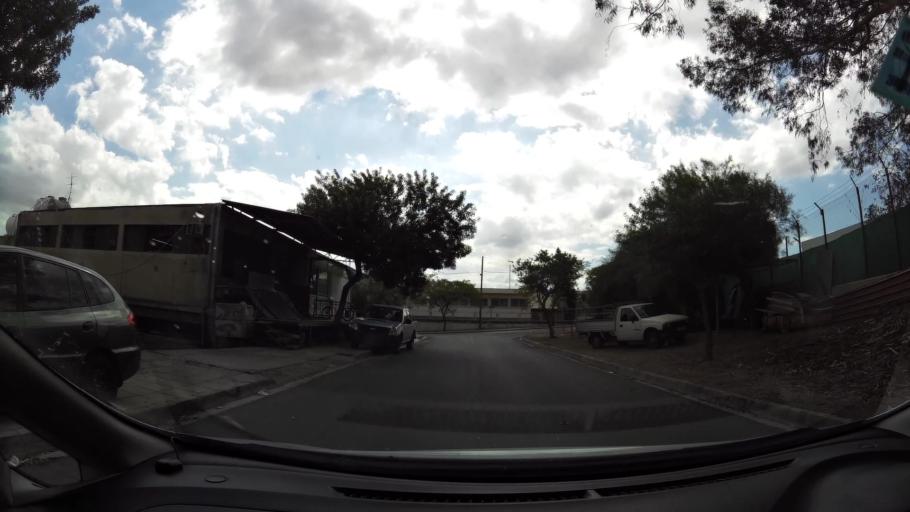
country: CY
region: Lefkosia
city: Nicosia
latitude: 35.1795
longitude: 33.3904
